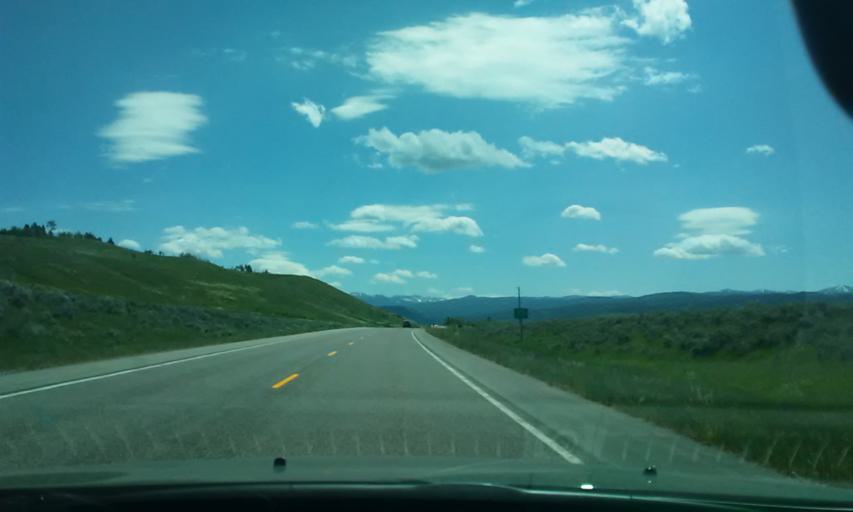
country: US
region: Wyoming
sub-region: Teton County
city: Jackson
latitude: 43.8401
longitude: -110.4560
